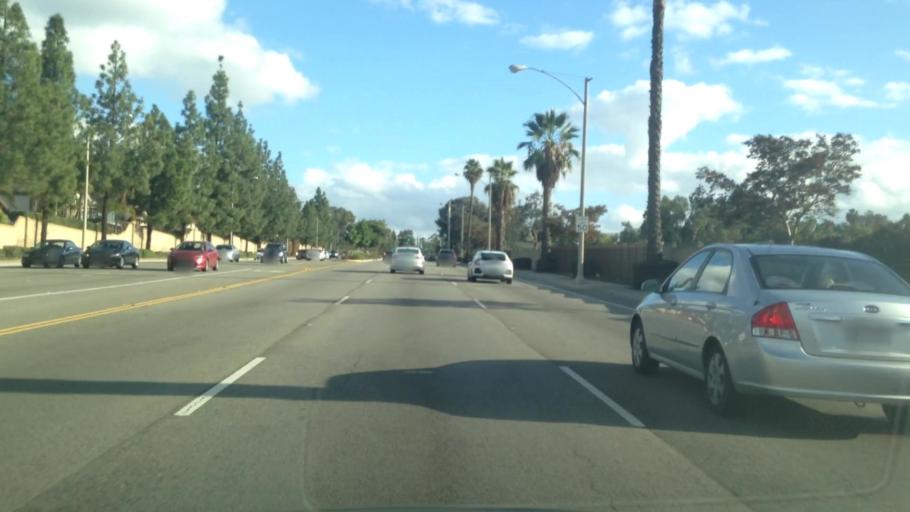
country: US
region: California
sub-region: Riverside County
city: Woodcrest
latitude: 33.9250
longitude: -117.3389
